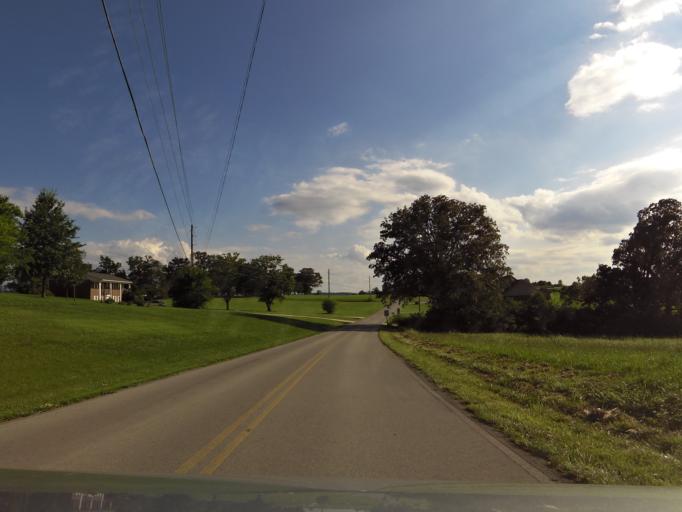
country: US
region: Tennessee
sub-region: Blount County
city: Maryville
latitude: 35.6824
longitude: -84.0491
